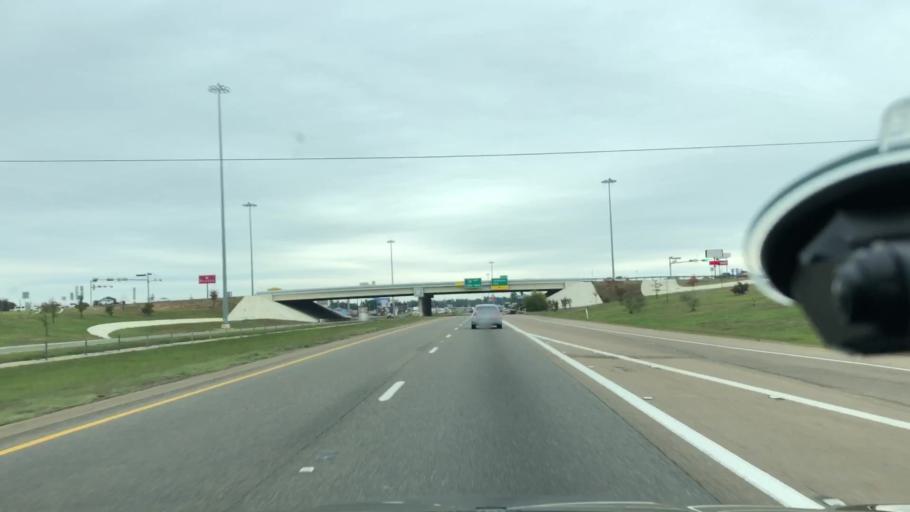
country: US
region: Arkansas
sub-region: Miller County
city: Texarkana
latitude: 33.4701
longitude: -94.0456
